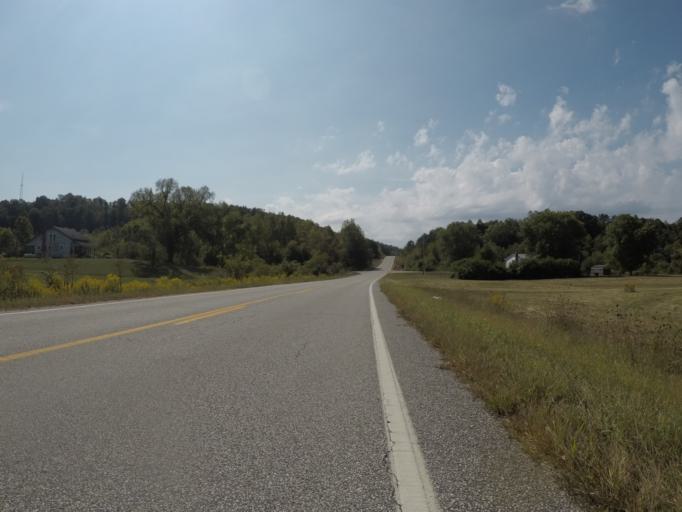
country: US
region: West Virginia
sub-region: Cabell County
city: Lesage
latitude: 38.5085
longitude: -82.3922
